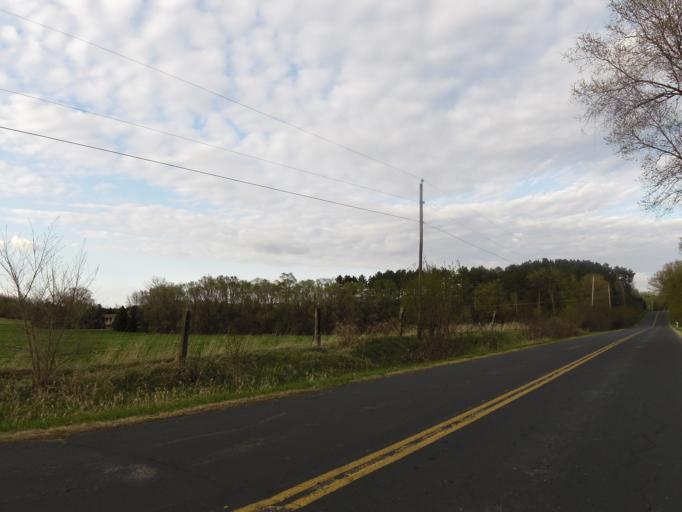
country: US
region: Minnesota
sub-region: Washington County
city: Lake Elmo
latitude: 44.9672
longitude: -92.8547
